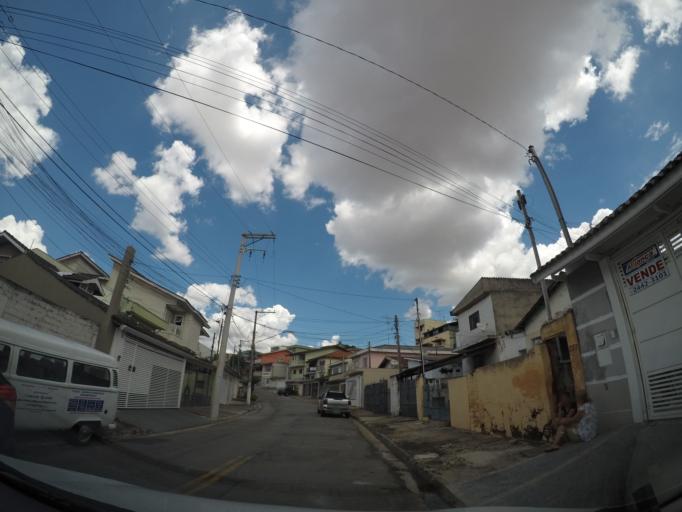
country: BR
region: Sao Paulo
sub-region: Guarulhos
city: Guarulhos
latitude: -23.4523
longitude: -46.5403
